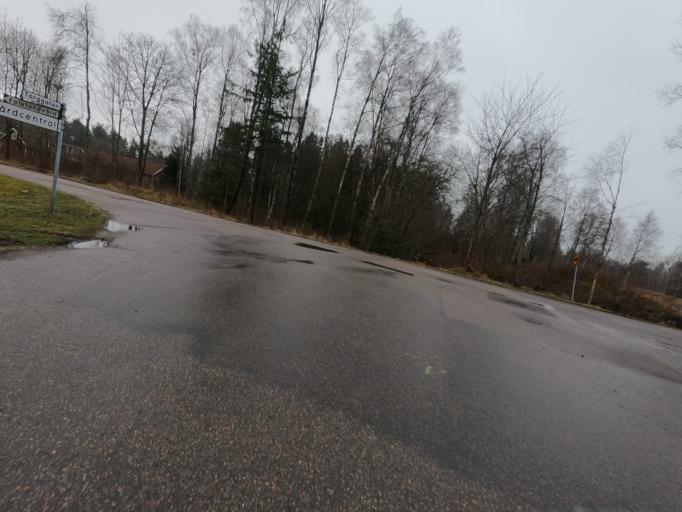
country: SE
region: Halland
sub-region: Hylte Kommun
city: Hyltebruk
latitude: 56.8269
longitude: 13.4367
